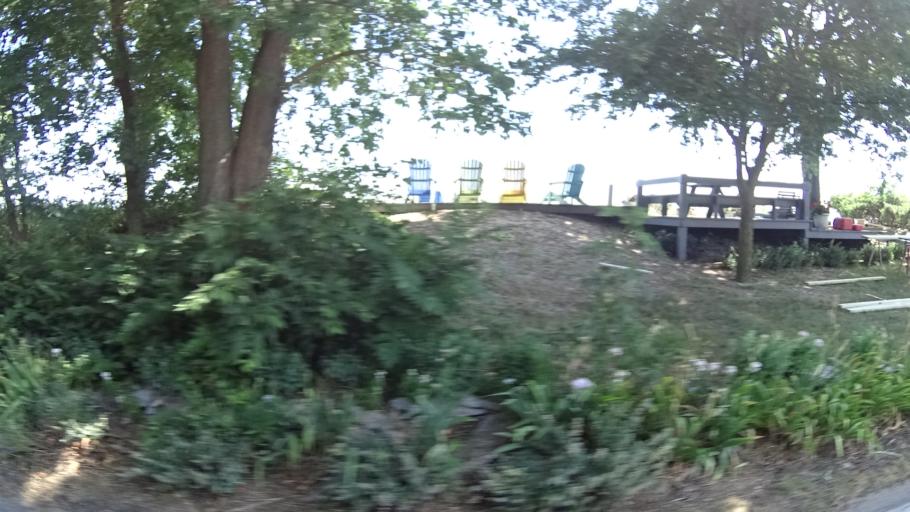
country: US
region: Ohio
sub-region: Erie County
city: Sandusky
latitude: 41.4494
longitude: -82.6445
